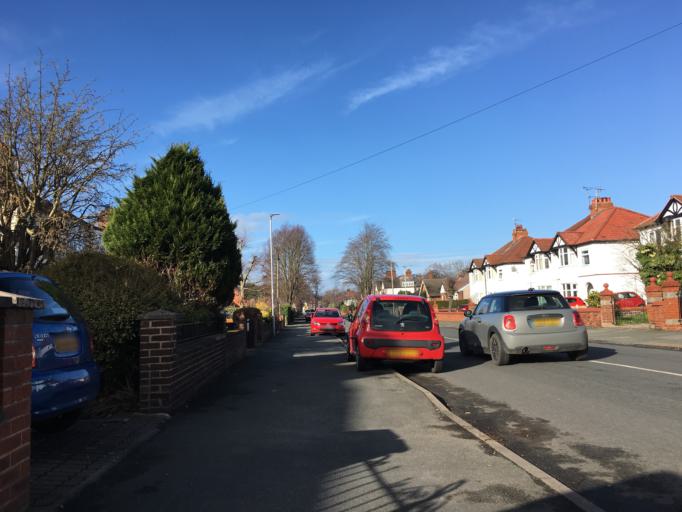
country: GB
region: England
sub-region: Cheshire West and Chester
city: Hoole
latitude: 53.1998
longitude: -2.8671
